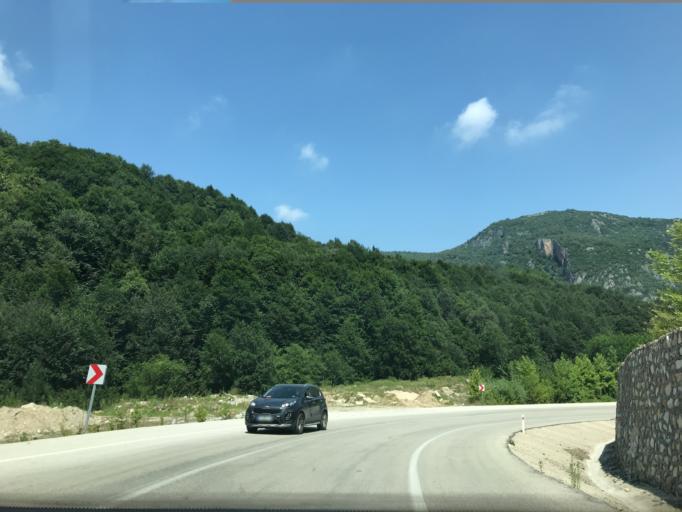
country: TR
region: Bursa
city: Tahtakopru
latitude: 39.9313
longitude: 29.5888
